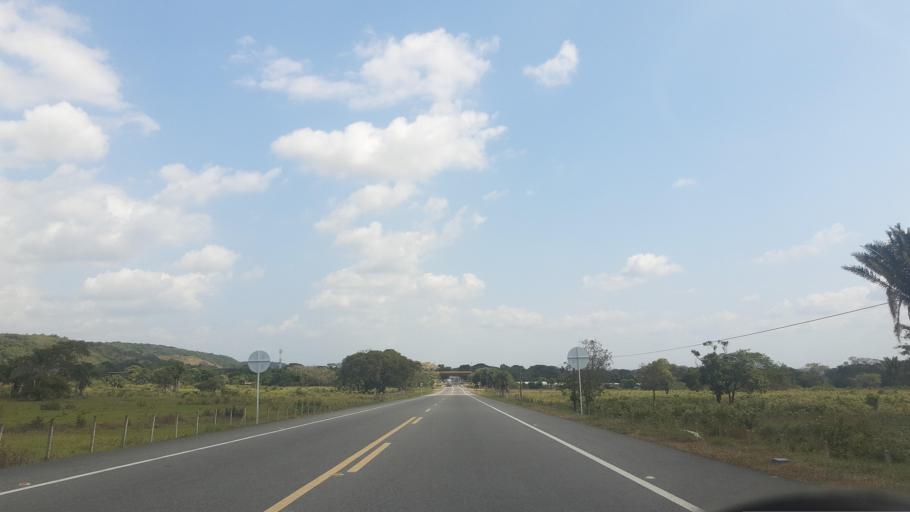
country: CO
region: Casanare
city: Tauramena
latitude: 4.8650
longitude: -72.7118
